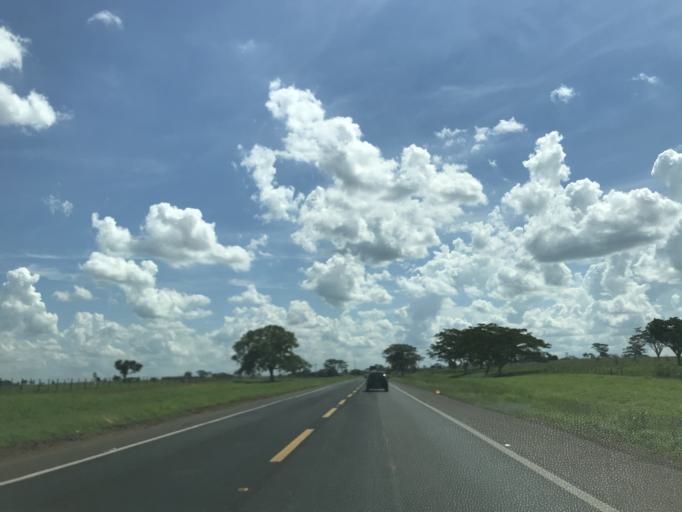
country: BR
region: Sao Paulo
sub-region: Nova Granada
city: Nova Granada
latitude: -20.4860
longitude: -49.3055
